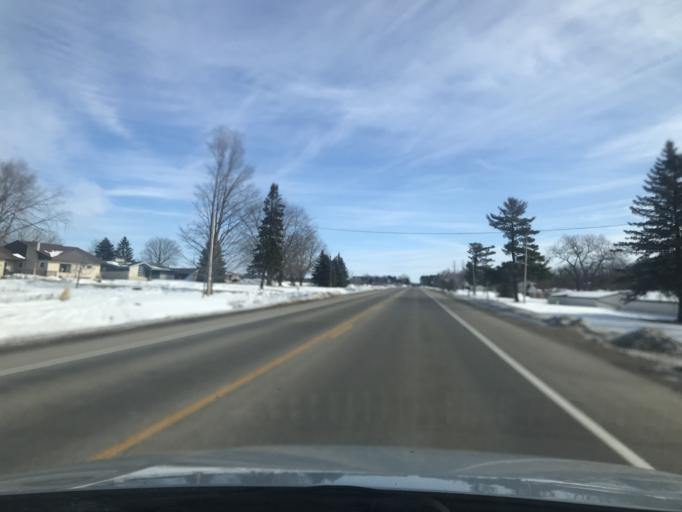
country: US
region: Wisconsin
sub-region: Oconto County
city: Gillett
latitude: 44.8969
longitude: -88.3029
